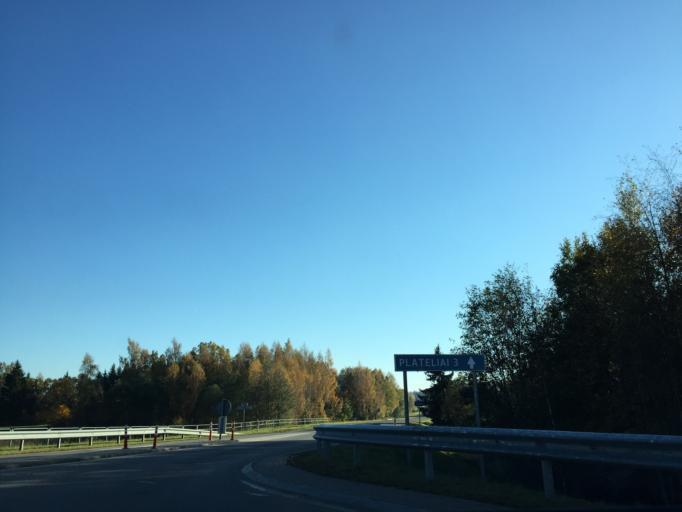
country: LT
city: Plateliai
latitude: 56.0709
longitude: 21.8232
